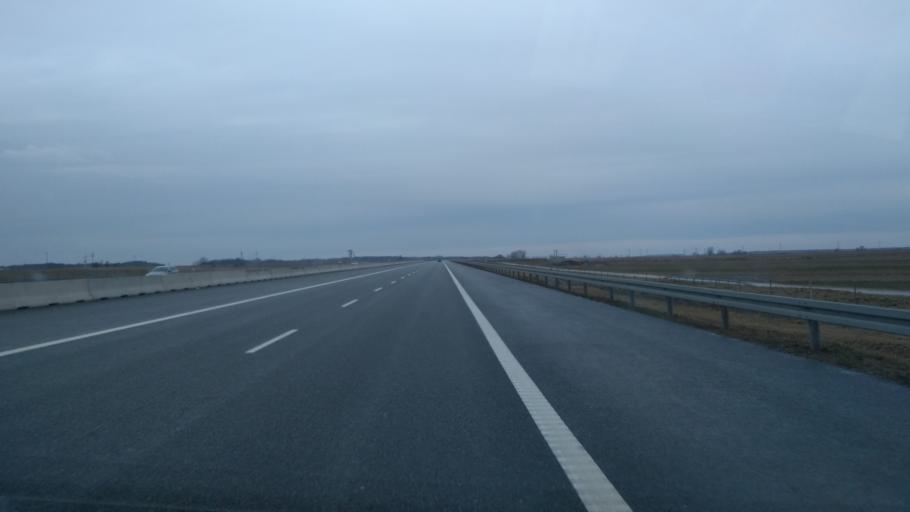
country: PL
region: Subcarpathian Voivodeship
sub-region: Powiat debicki
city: Czarna
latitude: 50.1012
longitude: 21.2477
